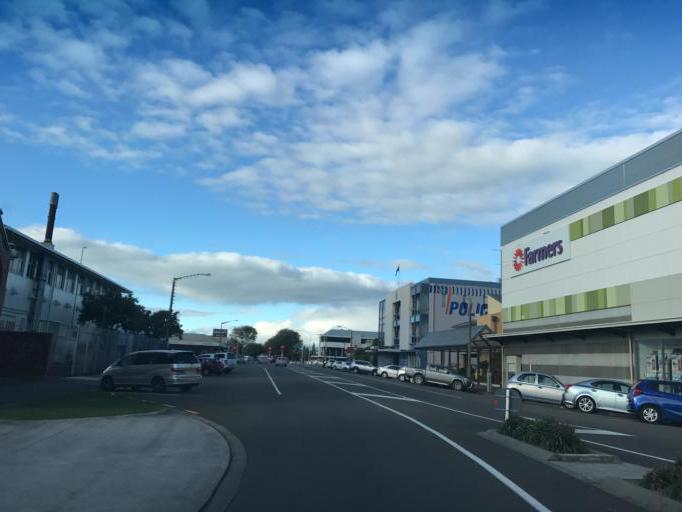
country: NZ
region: Manawatu-Wanganui
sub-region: Palmerston North City
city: Palmerston North
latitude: -40.3561
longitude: 175.6146
